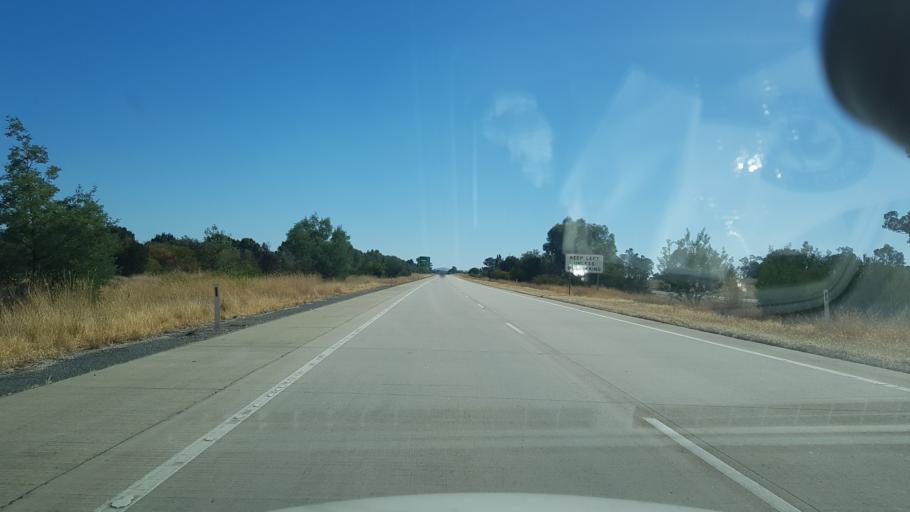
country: AU
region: New South Wales
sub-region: Greater Hume Shire
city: Jindera
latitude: -35.9253
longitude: 147.0294
